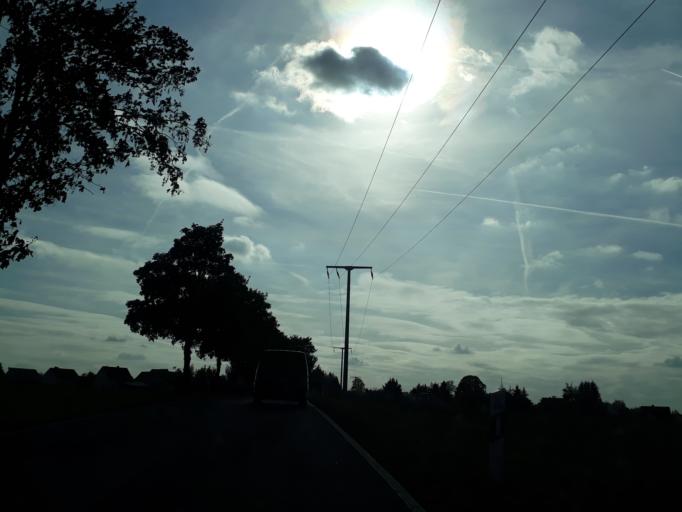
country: DE
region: Saxony
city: Wilsdruff
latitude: 51.0719
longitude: 13.5759
